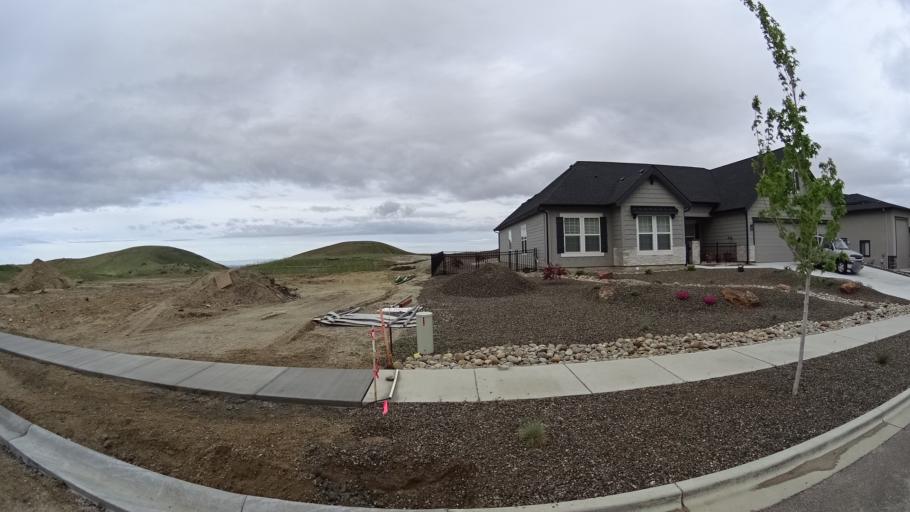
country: US
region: Idaho
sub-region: Ada County
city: Eagle
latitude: 43.7694
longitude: -116.2538
